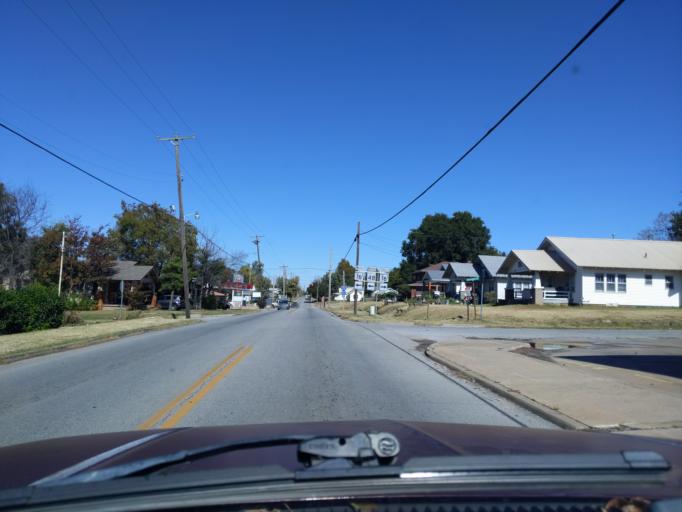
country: US
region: Oklahoma
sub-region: Creek County
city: Bristow
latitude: 35.8271
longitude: -96.3872
